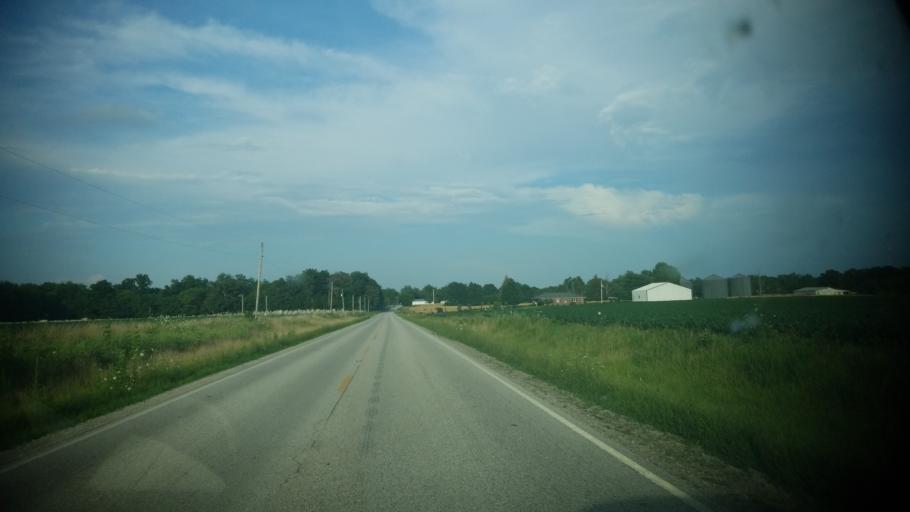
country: US
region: Illinois
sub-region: Clay County
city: Flora
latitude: 38.5160
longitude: -88.4516
